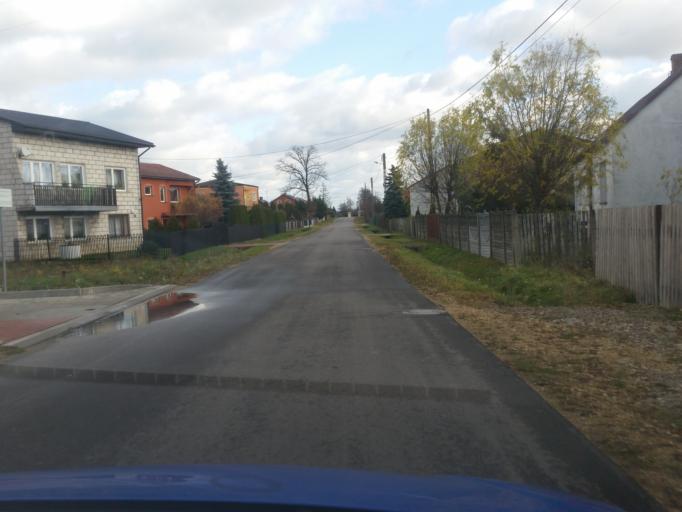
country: PL
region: Silesian Voivodeship
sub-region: Powiat czestochowski
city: Klomnice
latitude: 50.9622
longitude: 19.3333
